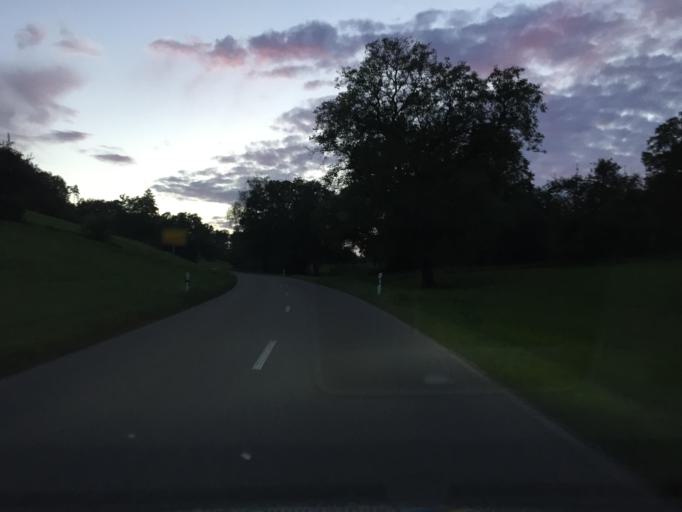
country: DE
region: Baden-Wuerttemberg
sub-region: Freiburg Region
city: Eggingen
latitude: 47.6628
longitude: 8.4187
